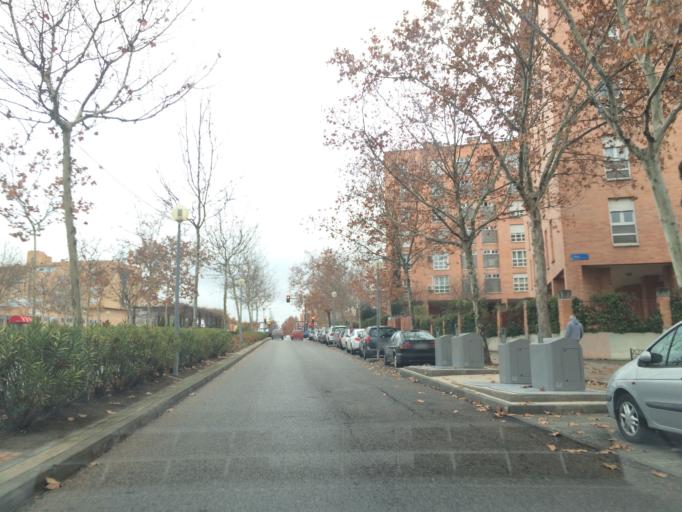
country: ES
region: Madrid
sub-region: Provincia de Madrid
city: Tres Cantos
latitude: 40.6010
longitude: -3.7132
